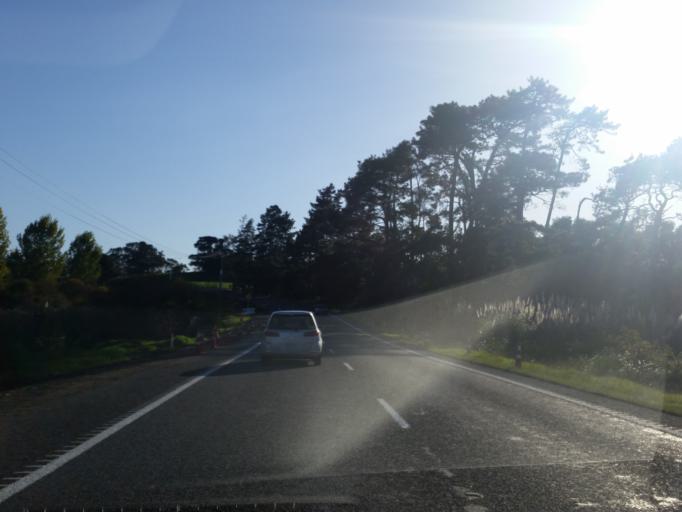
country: NZ
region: Bay of Plenty
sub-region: Western Bay of Plenty District
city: Waihi Beach
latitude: -37.4660
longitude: 175.9367
